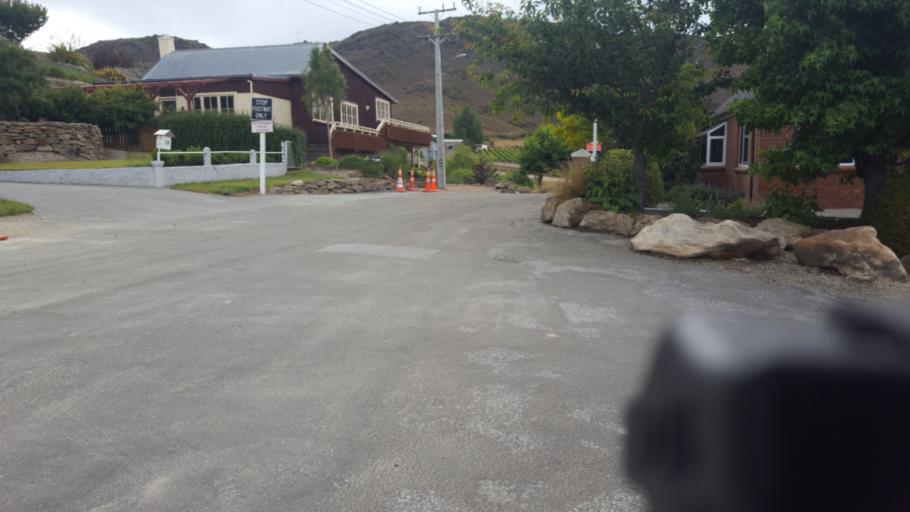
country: NZ
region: Otago
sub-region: Queenstown-Lakes District
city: Wanaka
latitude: -45.2533
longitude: 169.3981
